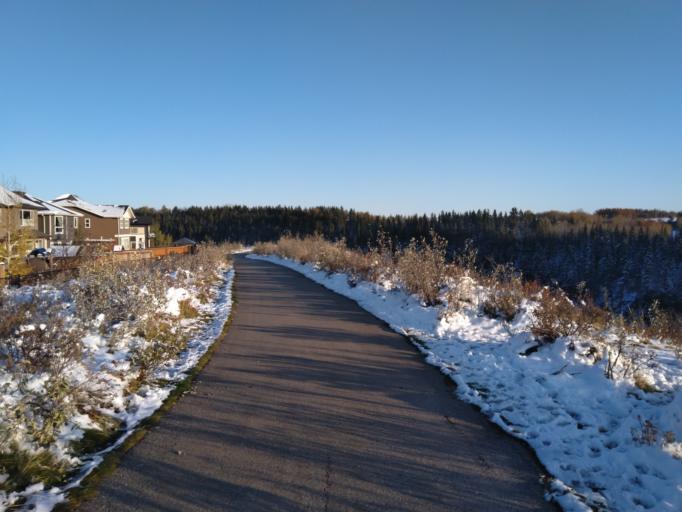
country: CA
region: Alberta
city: Cochrane
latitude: 51.1817
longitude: -114.5070
